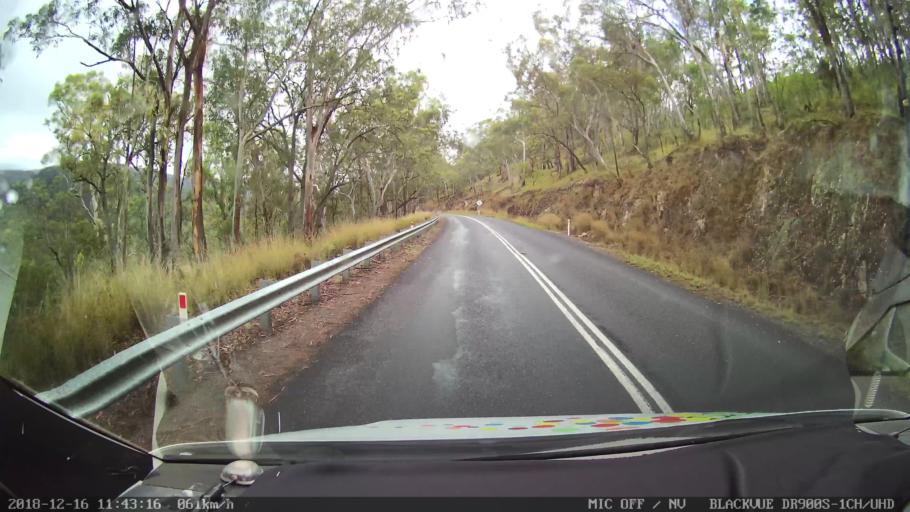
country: AU
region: New South Wales
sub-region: Tenterfield Municipality
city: Carrolls Creek
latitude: -28.9466
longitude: 152.2159
